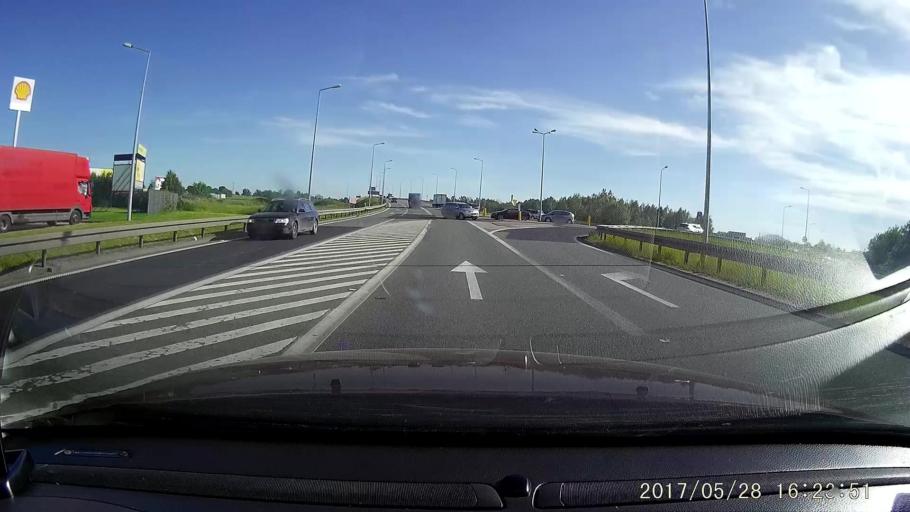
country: PL
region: Lower Silesian Voivodeship
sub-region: Powiat zgorzelecki
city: Lagow
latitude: 51.1768
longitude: 15.0311
